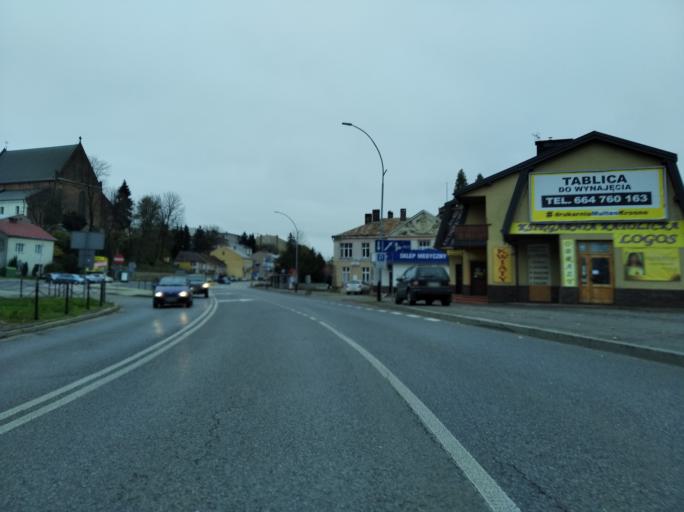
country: PL
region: Subcarpathian Voivodeship
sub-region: Krosno
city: Krosno
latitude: 49.6953
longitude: 21.7614
